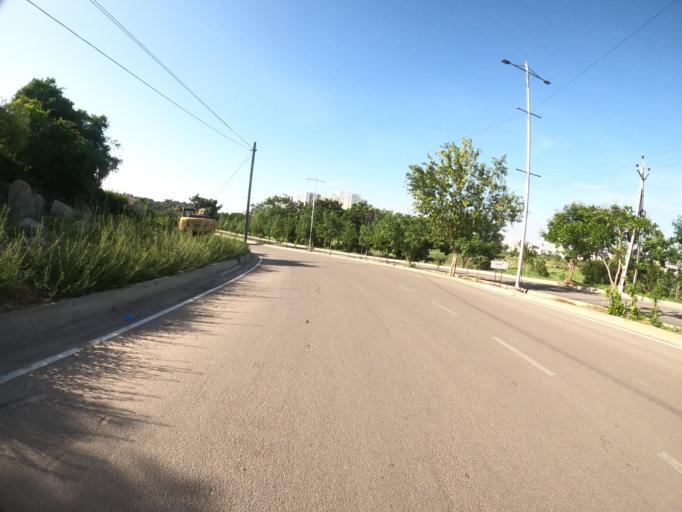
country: IN
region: Telangana
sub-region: Hyderabad
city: Hyderabad
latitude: 17.3543
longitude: 78.3698
